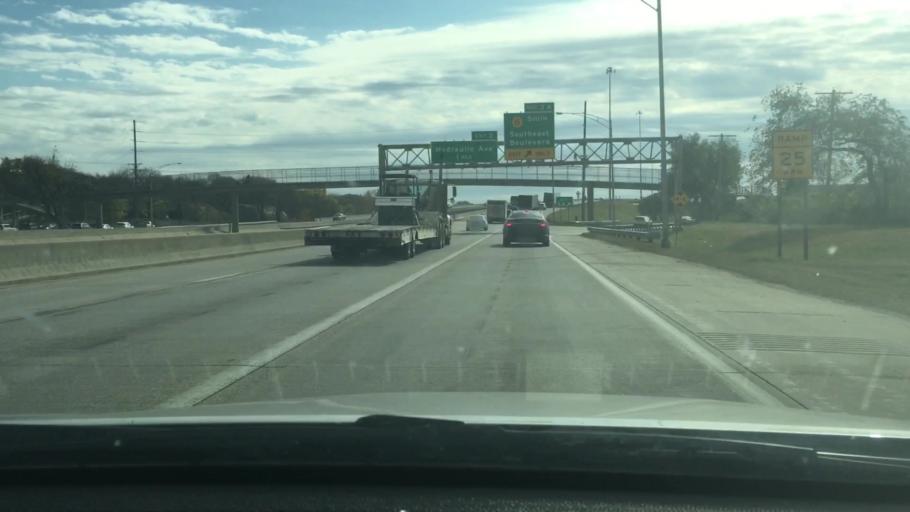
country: US
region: Kansas
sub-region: Sedgwick County
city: Wichita
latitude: 37.6436
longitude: -97.3087
